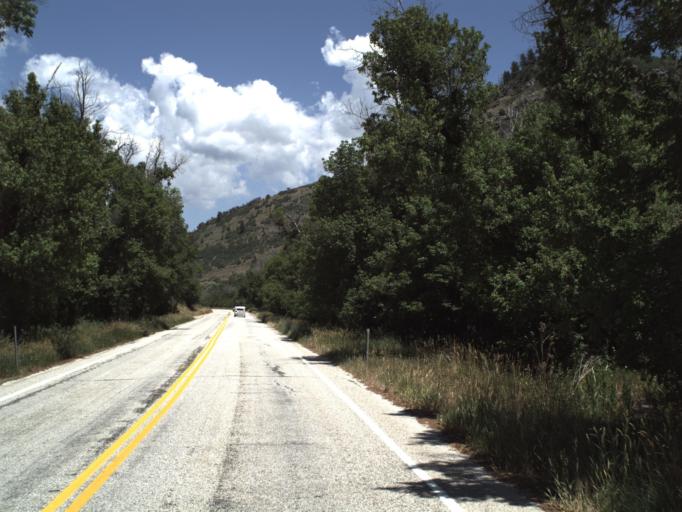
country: US
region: Utah
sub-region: Weber County
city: Wolf Creek
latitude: 41.2697
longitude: -111.6693
